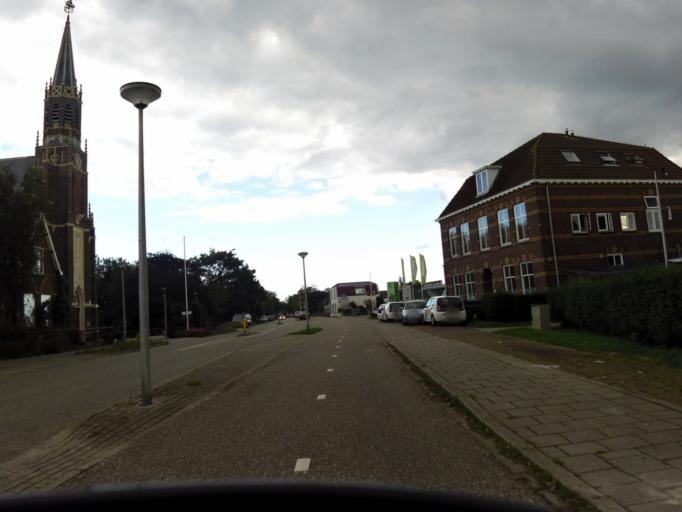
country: NL
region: South Holland
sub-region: Gemeente Leiderdorp
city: Leiderdorp
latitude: 52.1316
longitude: 4.5588
